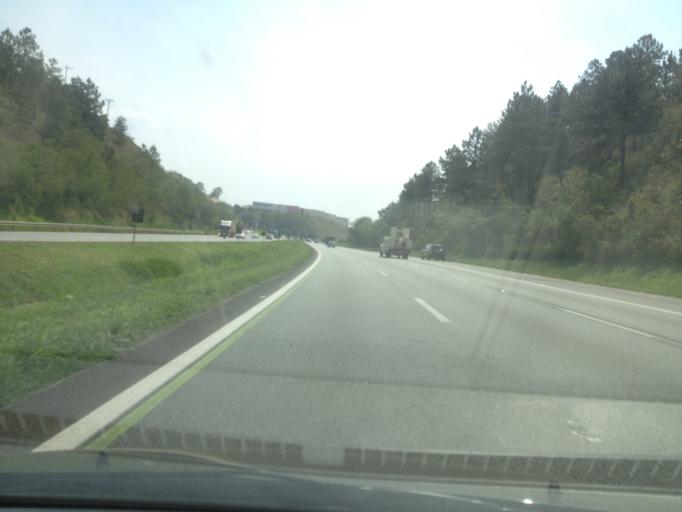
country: BR
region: Sao Paulo
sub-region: Sao Roque
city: Sao Roque
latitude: -23.4287
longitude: -47.1334
